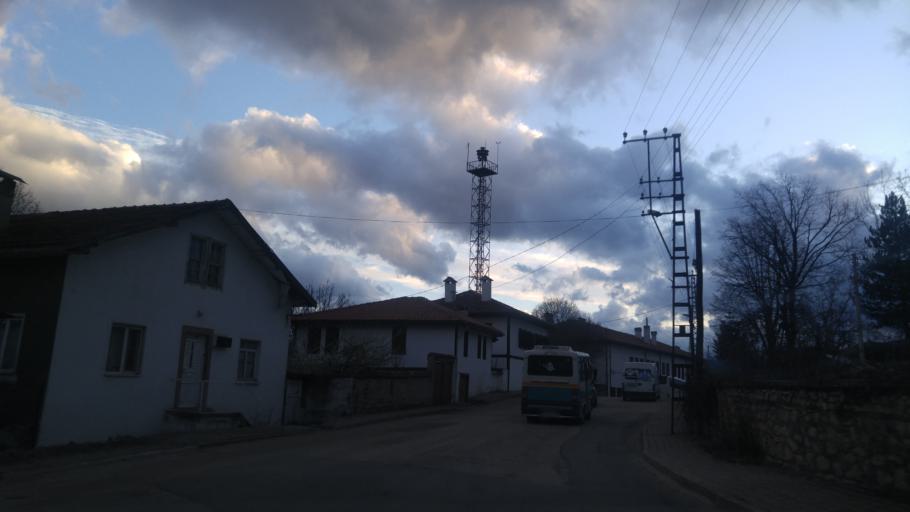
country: TR
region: Karabuk
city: Safranbolu
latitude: 41.2642
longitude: 32.6706
